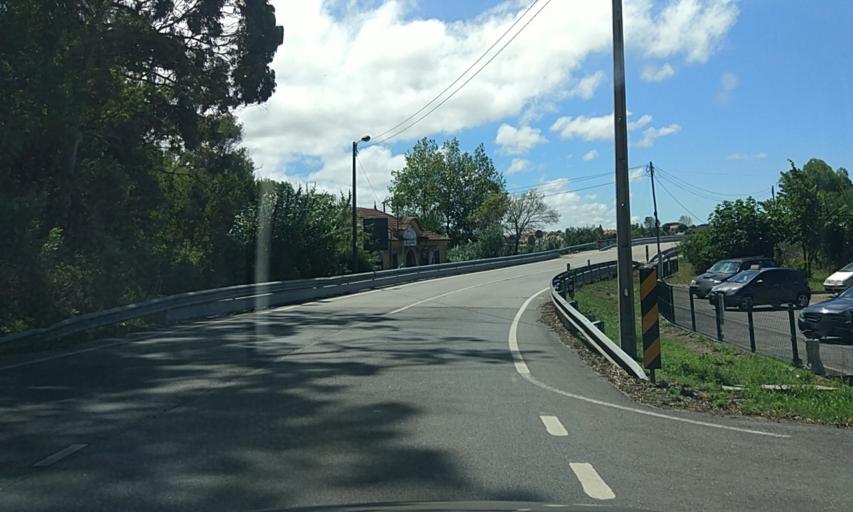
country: PT
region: Aveiro
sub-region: Vagos
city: Vagos
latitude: 40.5755
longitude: -8.6790
